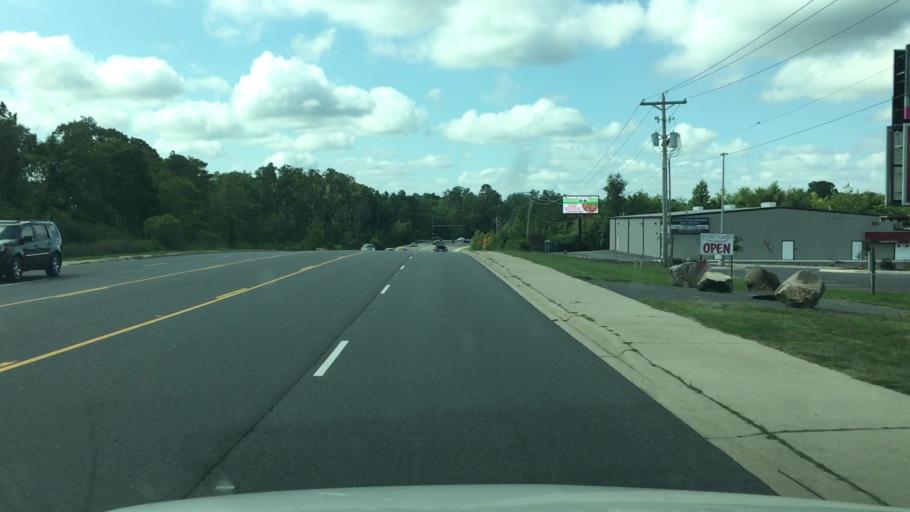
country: US
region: Arkansas
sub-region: Garland County
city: Lake Hamilton
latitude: 34.4579
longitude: -93.0774
